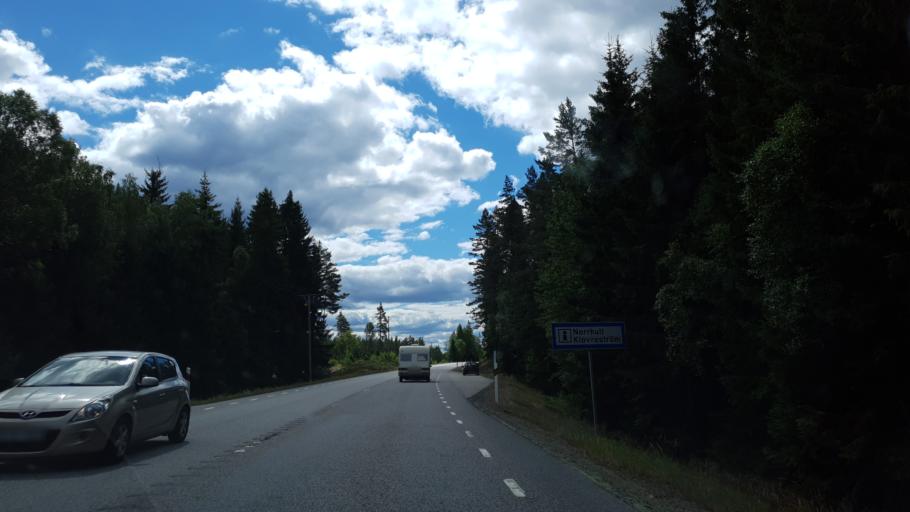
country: SE
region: Kronoberg
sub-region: Vaxjo Kommun
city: Braas
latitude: 57.1365
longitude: 15.1709
